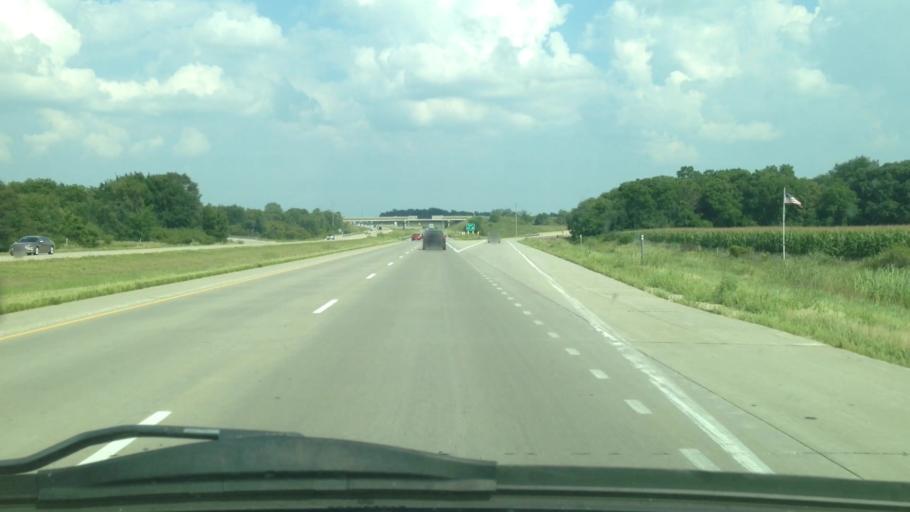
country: US
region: Iowa
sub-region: Black Hawk County
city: Elk Run Heights
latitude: 42.4501
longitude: -92.2272
